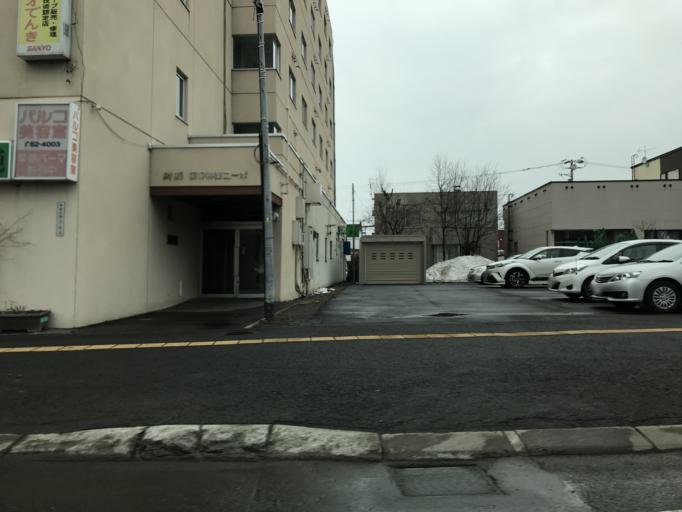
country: JP
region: Hokkaido
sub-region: Asahikawa-shi
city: Asahikawa
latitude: 43.7621
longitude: 142.3454
